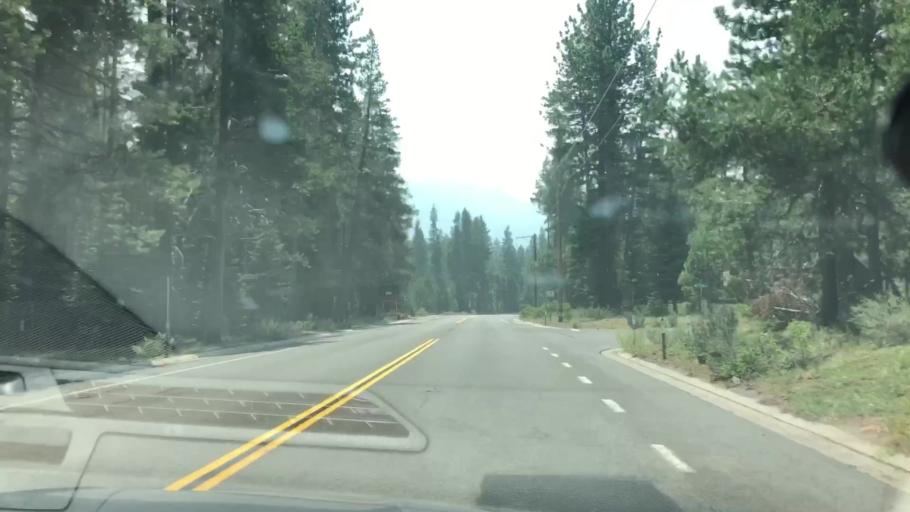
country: US
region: California
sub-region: El Dorado County
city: South Lake Tahoe
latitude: 38.8668
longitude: -119.9967
